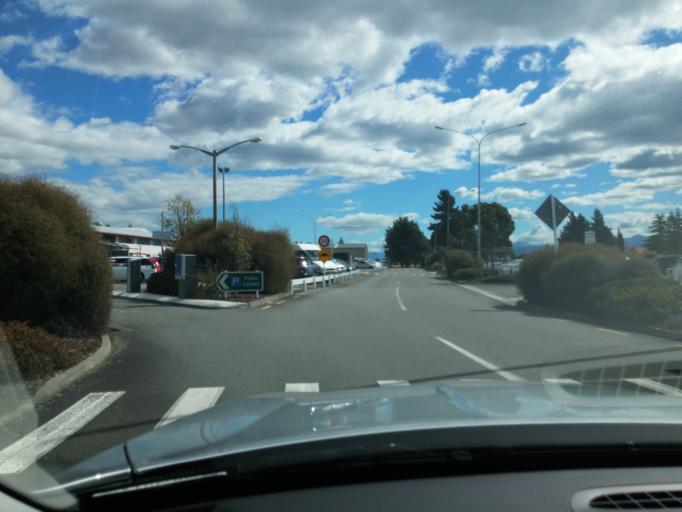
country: NZ
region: Marlborough
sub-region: Marlborough District
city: Blenheim
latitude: -41.5131
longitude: 173.8684
